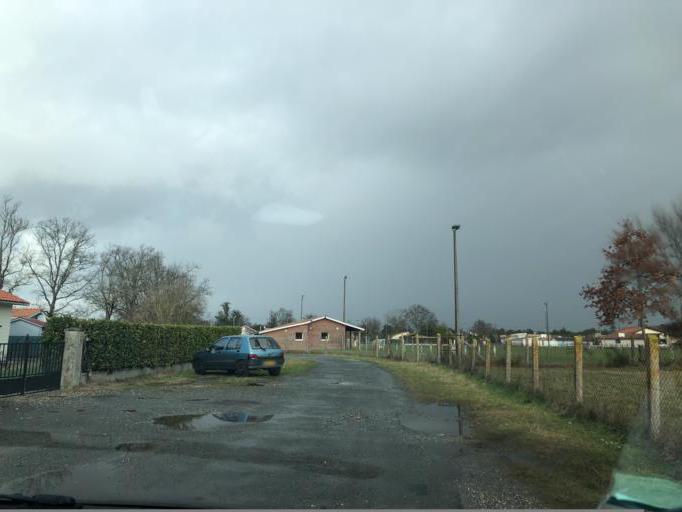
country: FR
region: Aquitaine
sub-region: Departement de la Gironde
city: Hourtin
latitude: 45.1837
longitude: -1.0528
